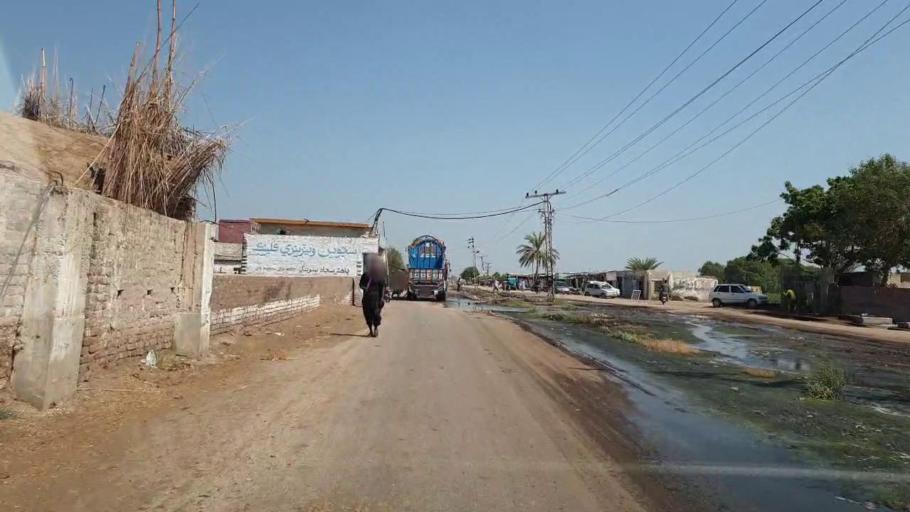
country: PK
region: Sindh
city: Hyderabad
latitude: 25.4231
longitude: 68.3903
